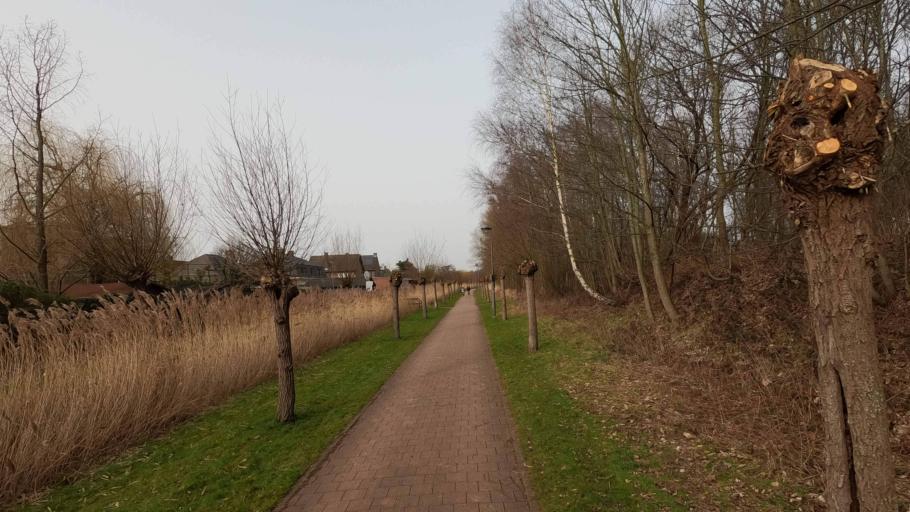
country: BE
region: Flanders
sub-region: Provincie Antwerpen
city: Zwijndrecht
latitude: 51.2204
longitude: 4.3413
